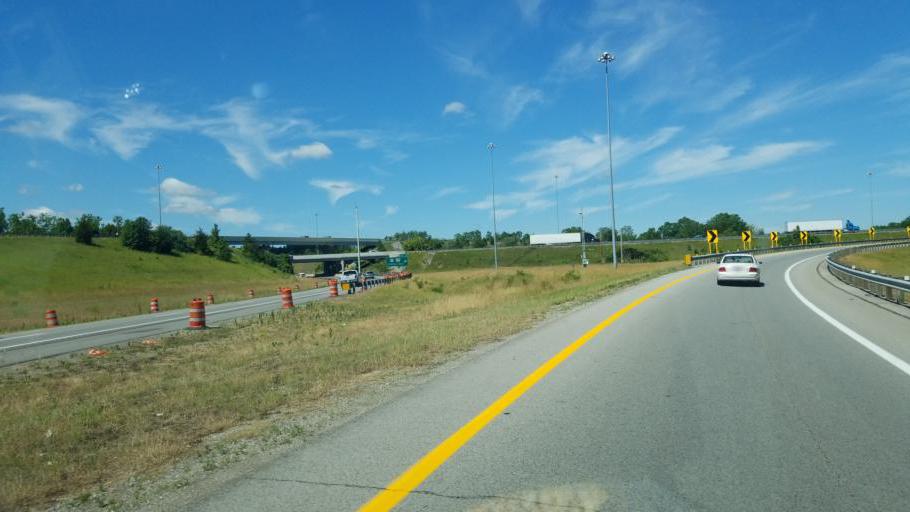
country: US
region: Ohio
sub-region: Lucas County
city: Sylvania
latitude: 41.6880
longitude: -83.6919
